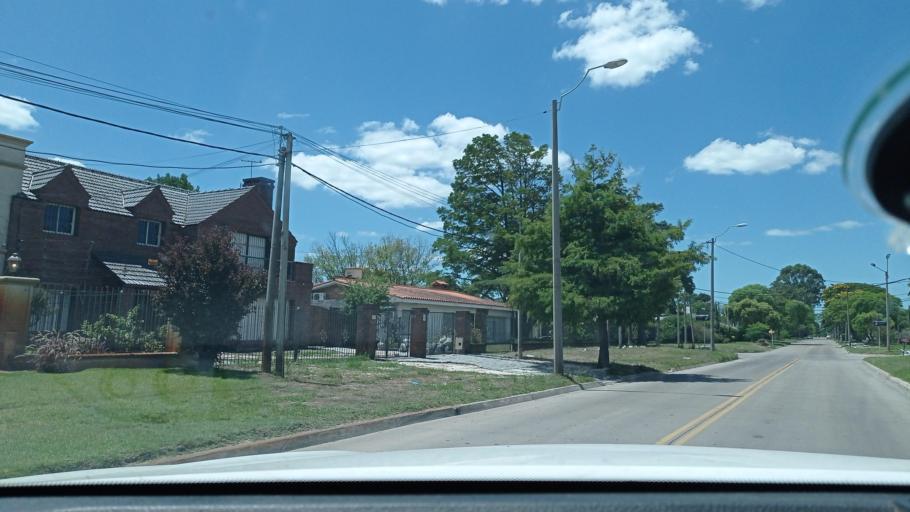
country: UY
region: Canelones
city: Paso de Carrasco
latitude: -34.8755
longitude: -56.0524
